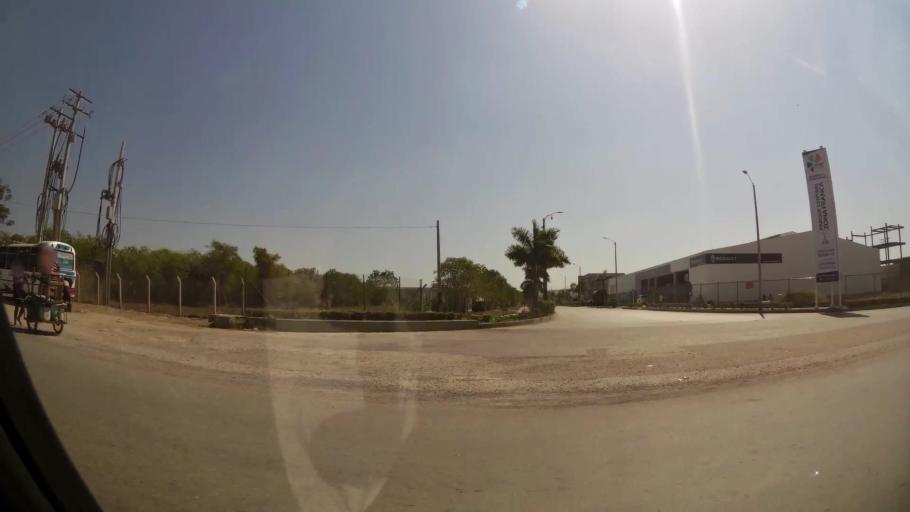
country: CO
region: Bolivar
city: Cartagena
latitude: 10.3893
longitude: -75.4491
